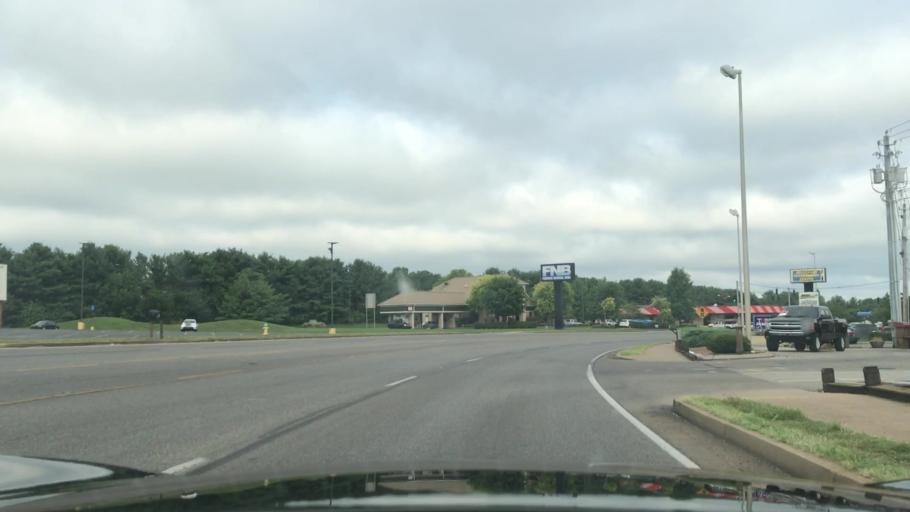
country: US
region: Kentucky
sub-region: Warren County
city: Bowling Green
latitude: 36.9509
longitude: -86.4397
